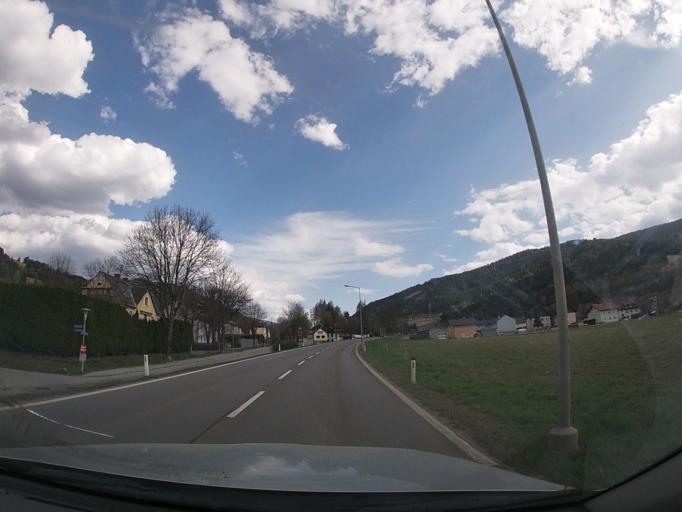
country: AT
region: Styria
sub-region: Politischer Bezirk Murau
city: Sankt Lorenzen bei Scheifling
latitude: 47.1479
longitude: 14.4153
